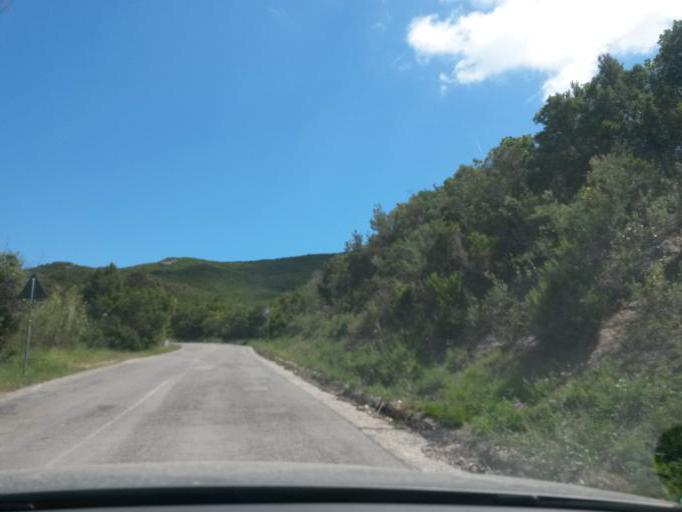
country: IT
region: Tuscany
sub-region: Provincia di Livorno
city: Campo nell'Elba
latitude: 42.7615
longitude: 10.2634
